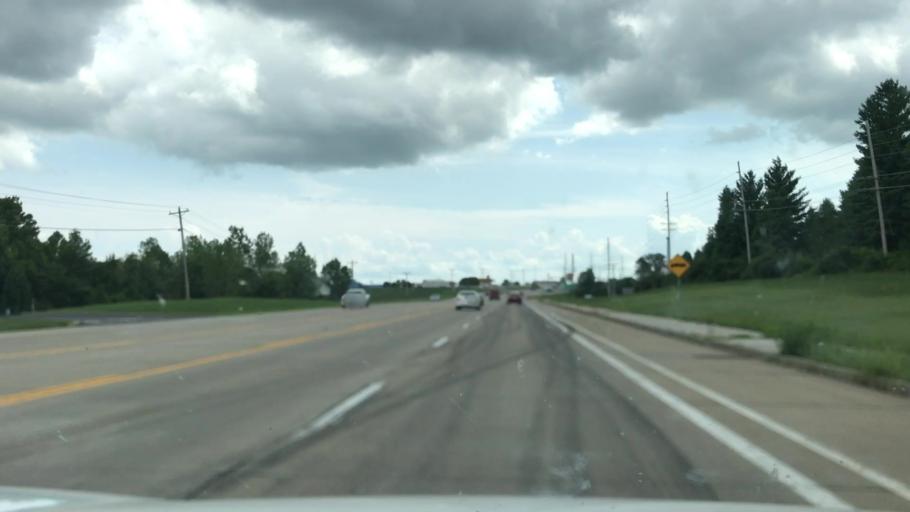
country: US
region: Missouri
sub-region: Saint Charles County
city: Weldon Spring
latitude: 38.7386
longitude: -90.6938
